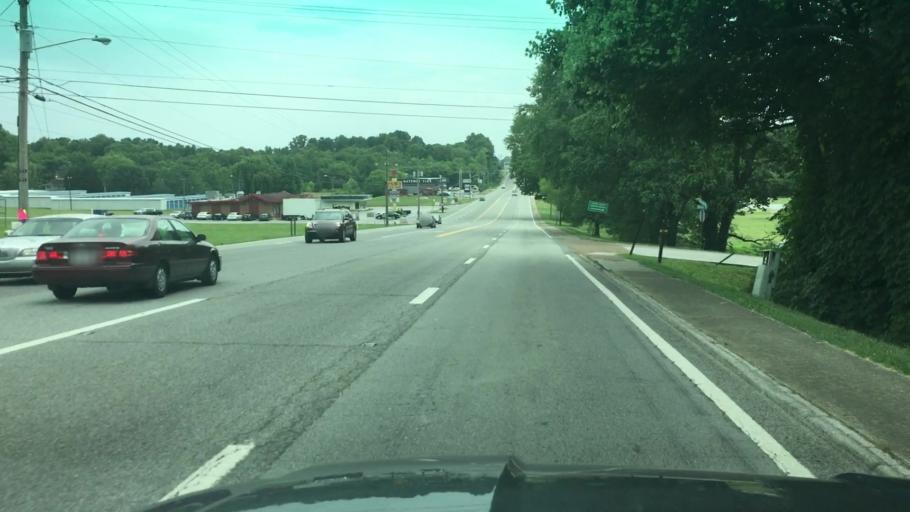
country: US
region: Tennessee
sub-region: Coffee County
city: Manchester
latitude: 35.4848
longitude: -86.0771
